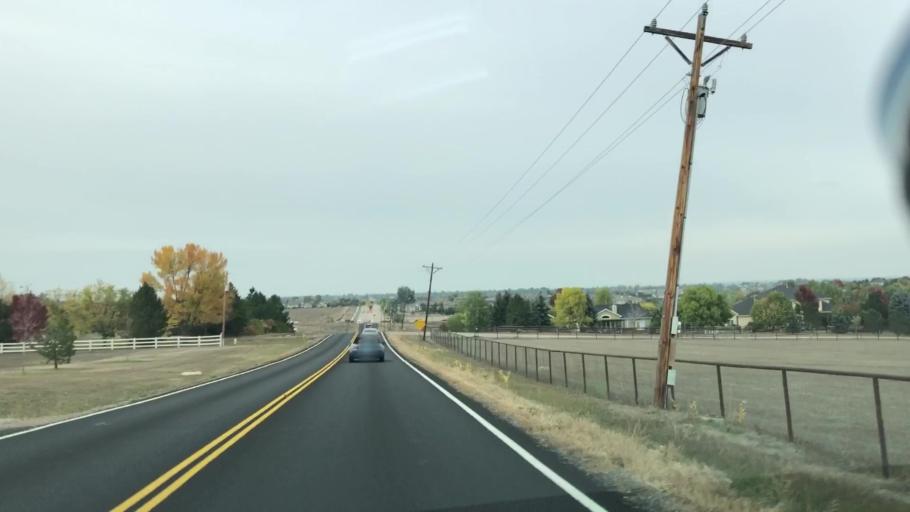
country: US
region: Colorado
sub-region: Larimer County
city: Loveland
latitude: 40.4755
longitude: -105.0583
